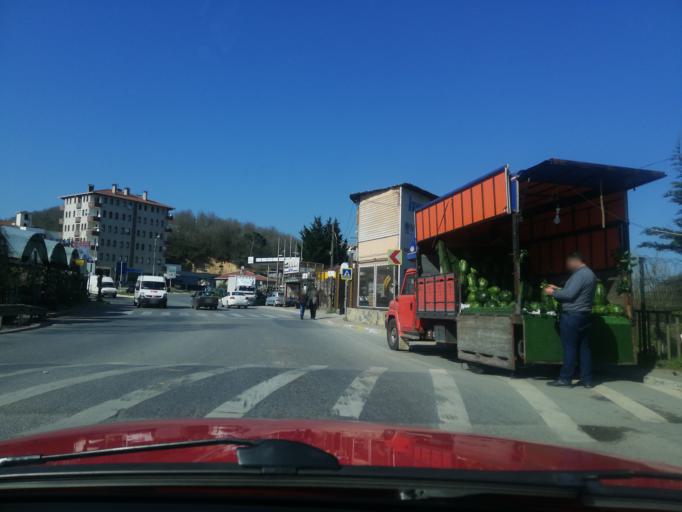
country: TR
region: Istanbul
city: Umraniye
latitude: 41.0855
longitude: 29.1362
